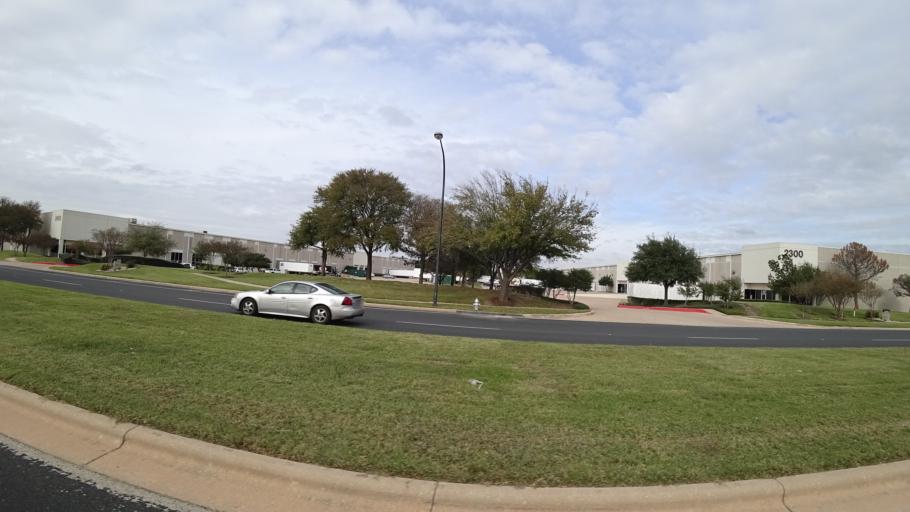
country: US
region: Texas
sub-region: Travis County
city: Wells Branch
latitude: 30.4571
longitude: -97.6755
